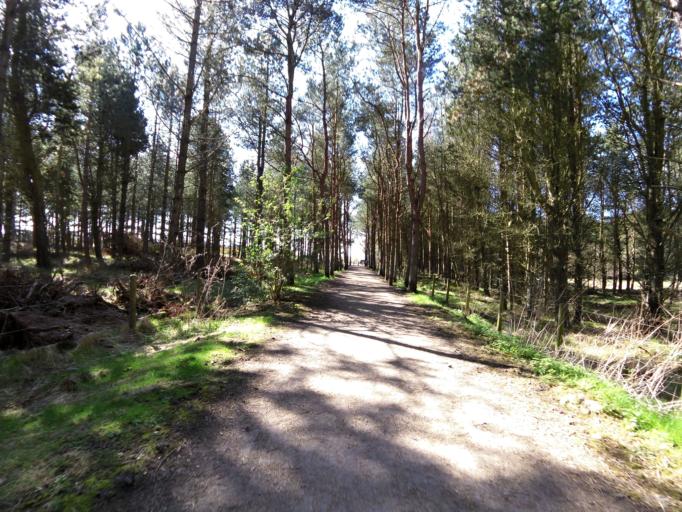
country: GB
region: Scotland
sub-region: Angus
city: Montrose
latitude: 56.7404
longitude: -2.4519
